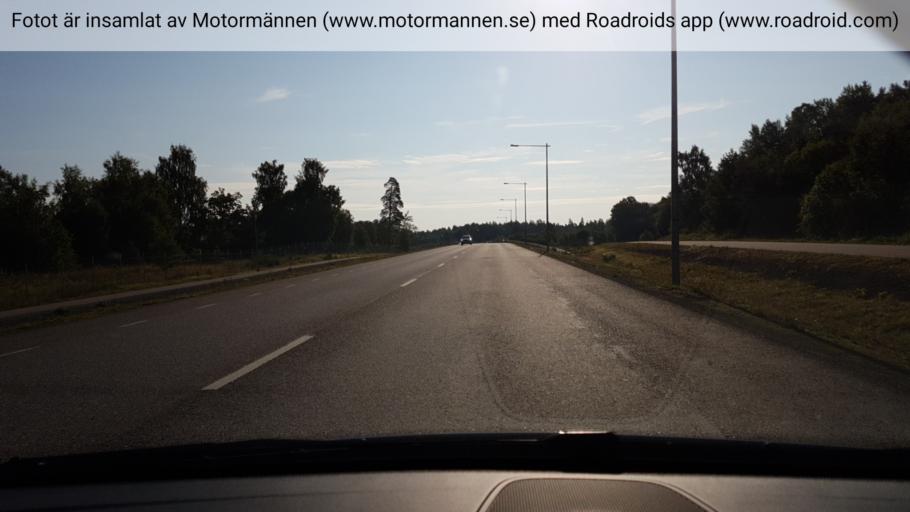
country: SE
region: Vaestra Goetaland
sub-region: Skovde Kommun
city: Skultorp
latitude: 58.3682
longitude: 13.8446
